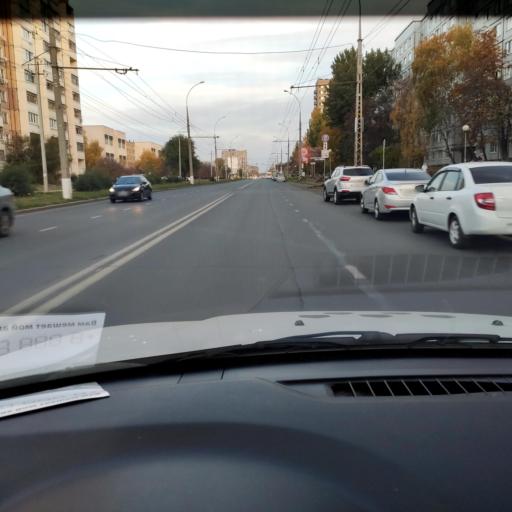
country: RU
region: Samara
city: Tol'yatti
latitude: 53.5356
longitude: 49.3057
